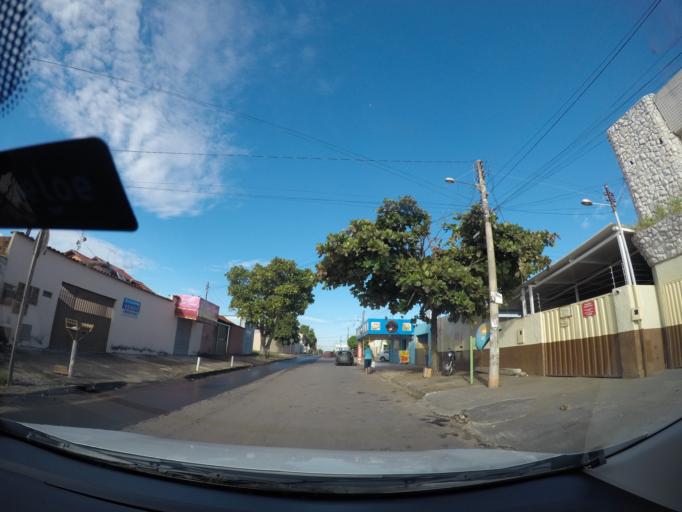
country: BR
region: Goias
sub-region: Aparecida De Goiania
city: Aparecida de Goiania
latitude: -16.7545
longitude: -49.2768
